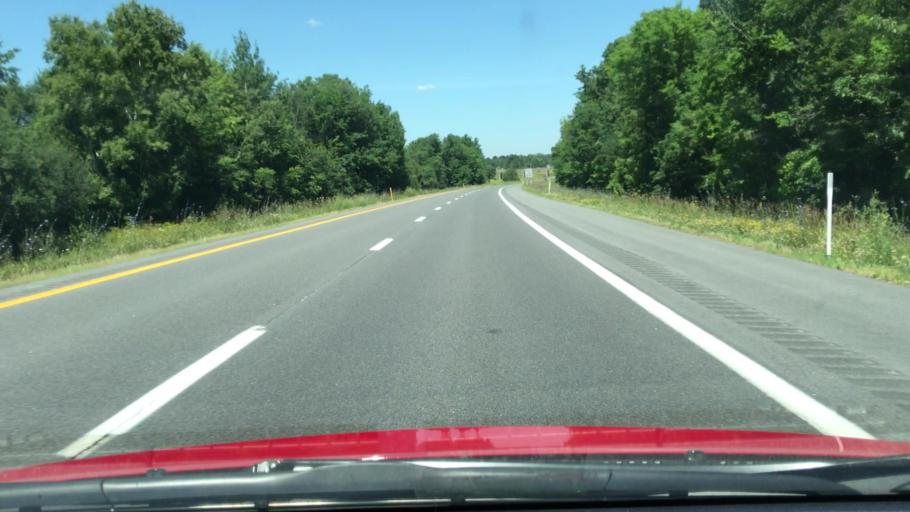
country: US
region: New York
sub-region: Clinton County
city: Cumberland Head
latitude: 44.8127
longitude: -73.4460
